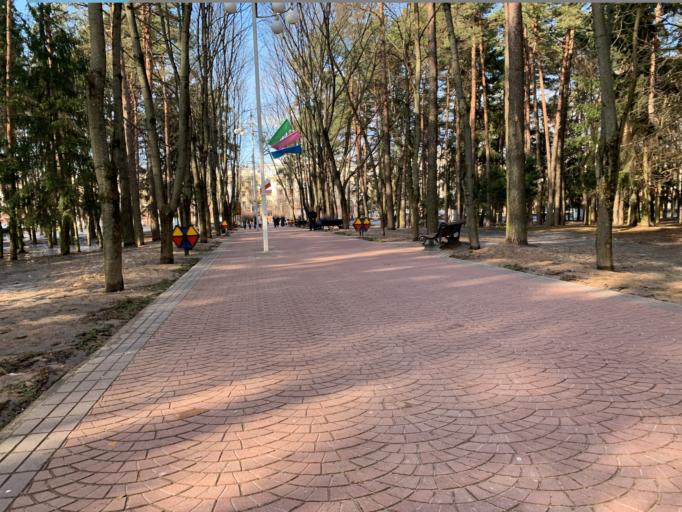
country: BY
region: Minsk
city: Minsk
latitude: 53.9223
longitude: 27.6119
